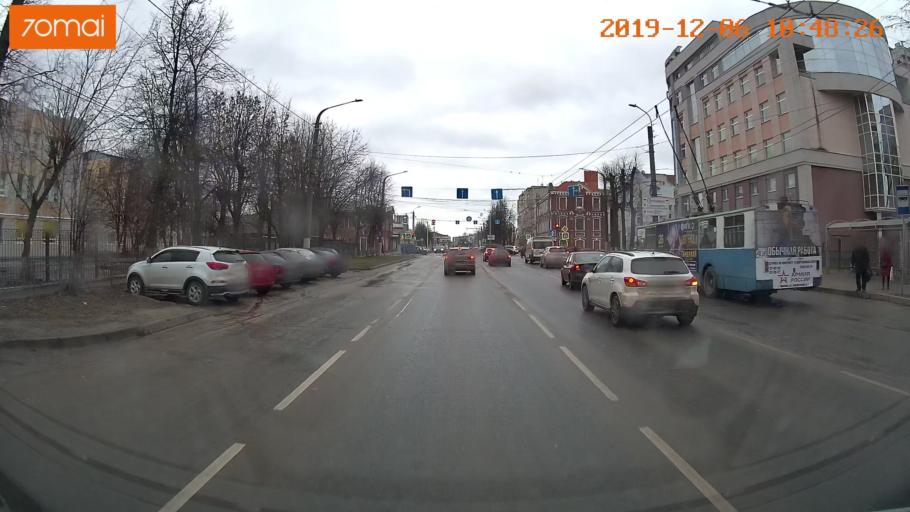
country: RU
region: Ivanovo
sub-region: Gorod Ivanovo
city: Ivanovo
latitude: 56.9952
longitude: 40.9699
